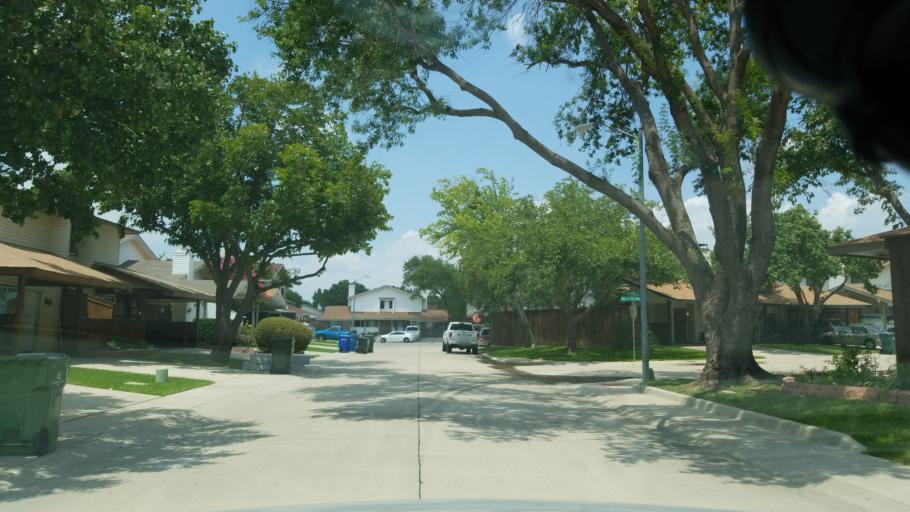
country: US
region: Texas
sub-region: Dallas County
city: Carrollton
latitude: 32.9672
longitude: -96.8660
